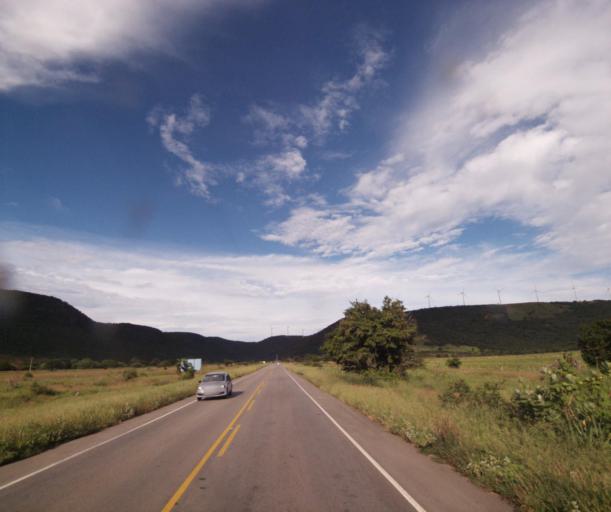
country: BR
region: Bahia
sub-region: Guanambi
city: Guanambi
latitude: -14.1621
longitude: -42.7165
